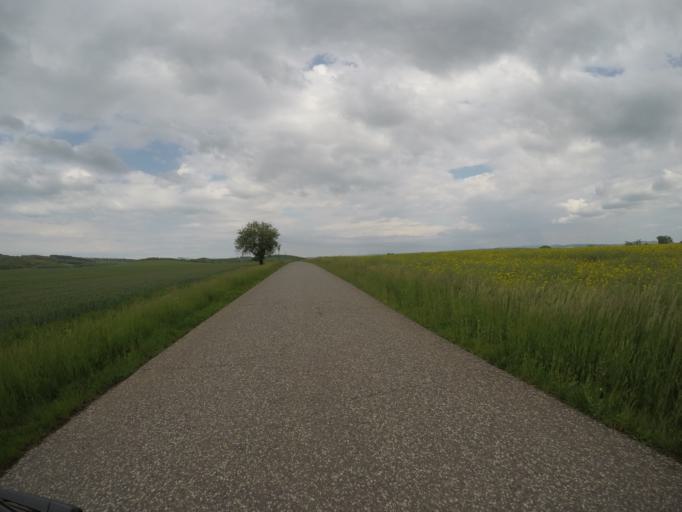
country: SK
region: Nitriansky
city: Sahy
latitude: 48.0682
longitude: 18.8587
